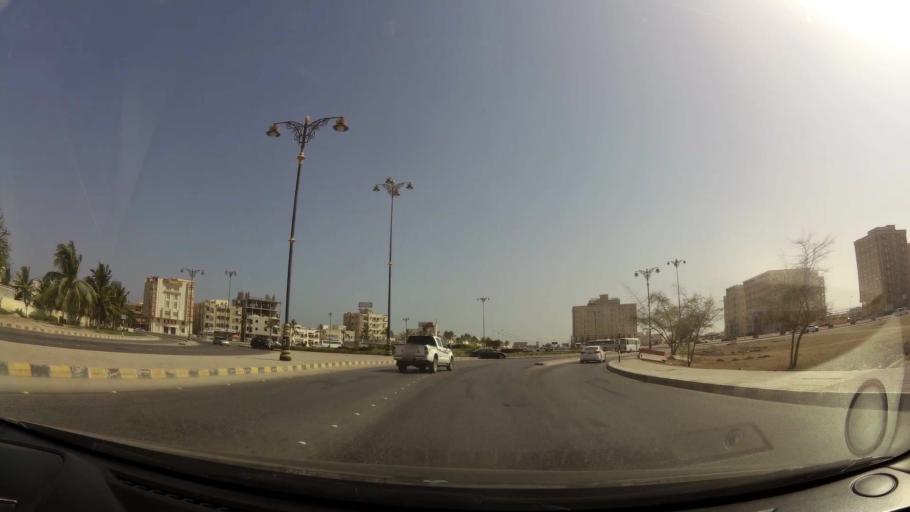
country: OM
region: Zufar
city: Salalah
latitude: 17.0059
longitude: 54.0410
